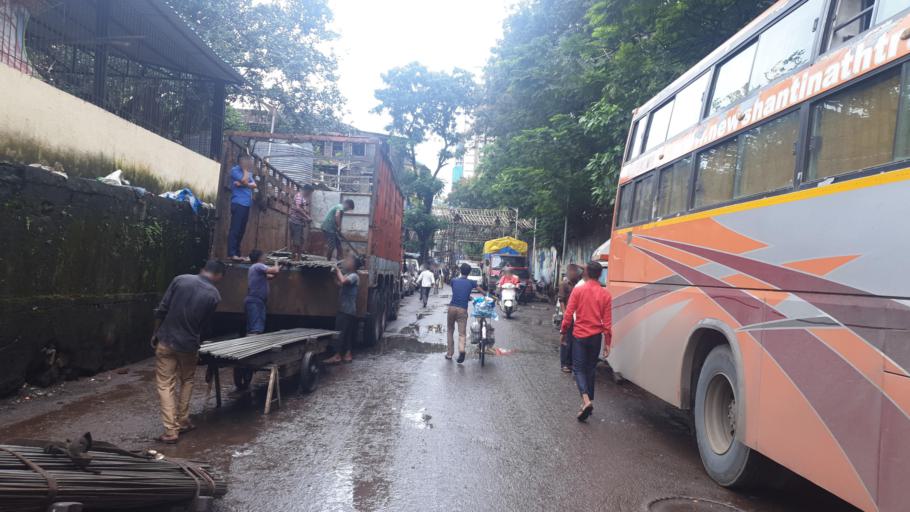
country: IN
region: Maharashtra
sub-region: Mumbai Suburban
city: Mumbai
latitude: 18.9614
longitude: 72.8273
